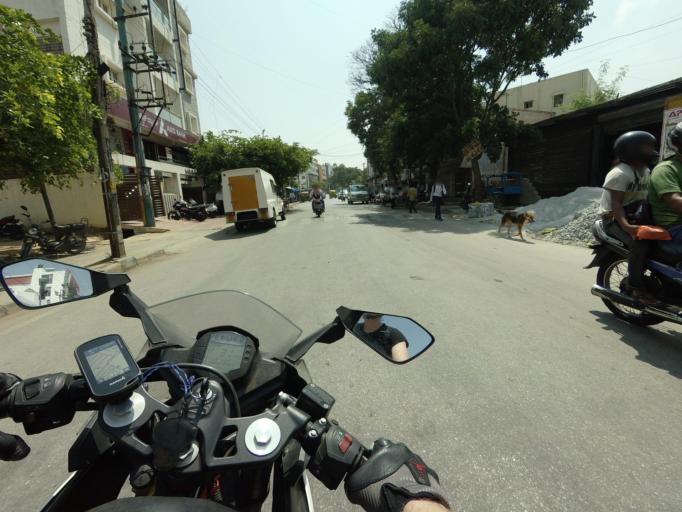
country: IN
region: Karnataka
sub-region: Bangalore Urban
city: Bangalore
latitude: 13.0102
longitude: 77.6576
